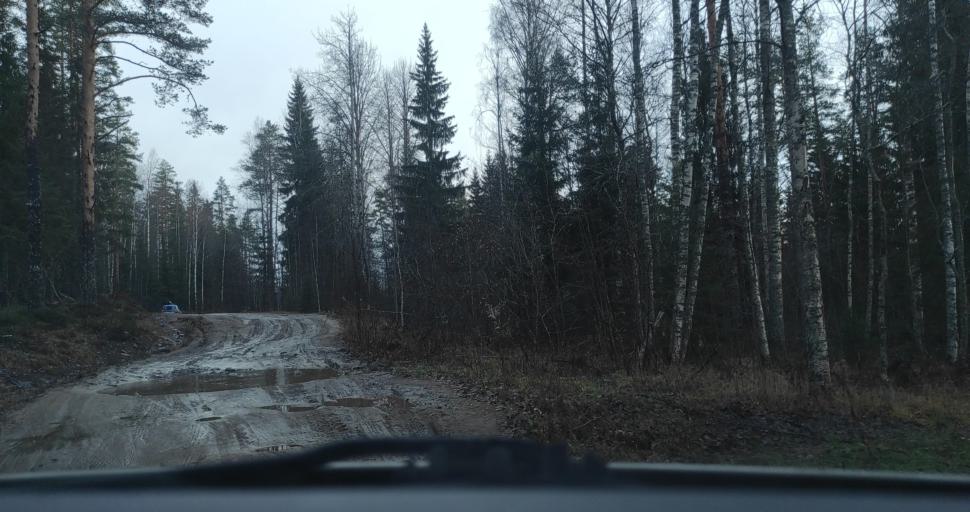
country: RU
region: Republic of Karelia
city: Pitkyaranta
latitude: 61.7445
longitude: 31.3945
